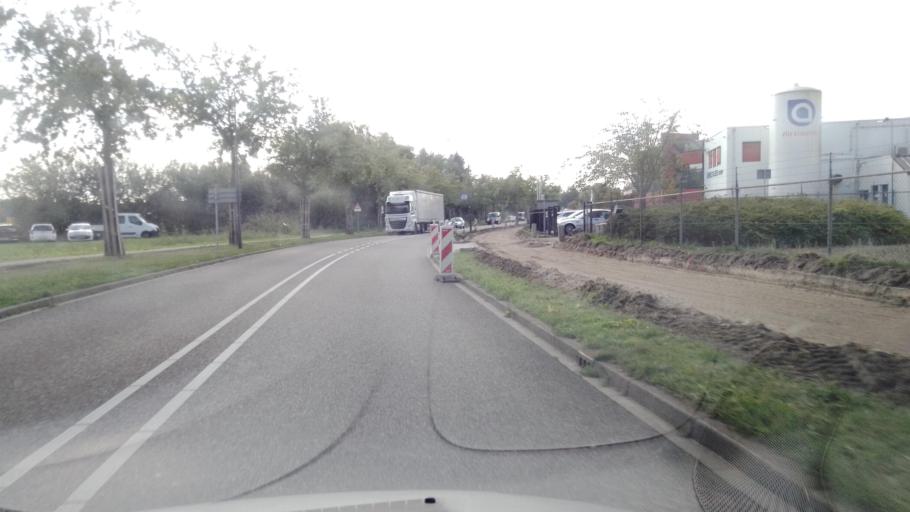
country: NL
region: North Brabant
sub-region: Gemeente Helmond
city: Helmond
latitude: 51.4568
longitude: 5.6915
